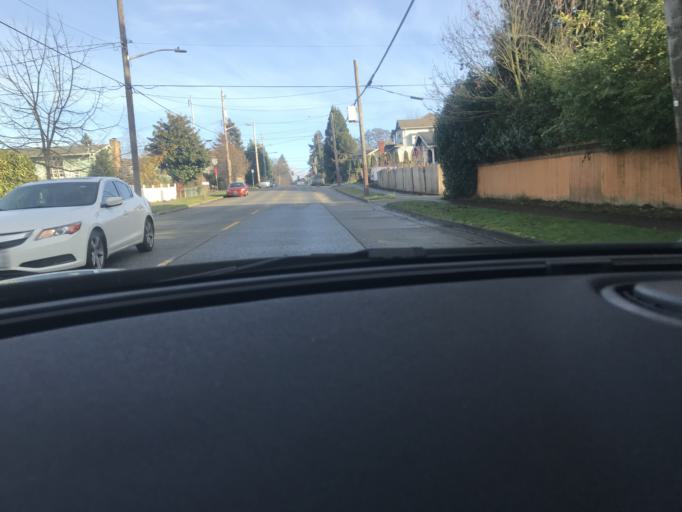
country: US
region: Washington
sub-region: King County
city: White Center
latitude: 47.5247
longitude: -122.3629
